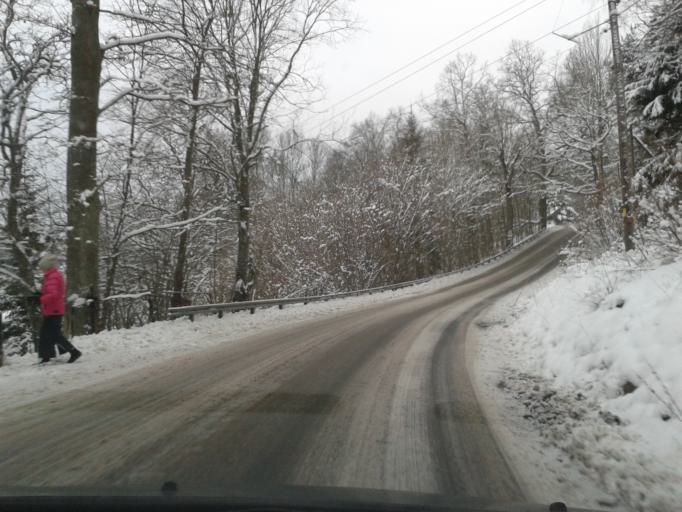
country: SE
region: Stockholm
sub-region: Nacka Kommun
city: Saltsjobaden
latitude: 59.2265
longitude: 18.3037
